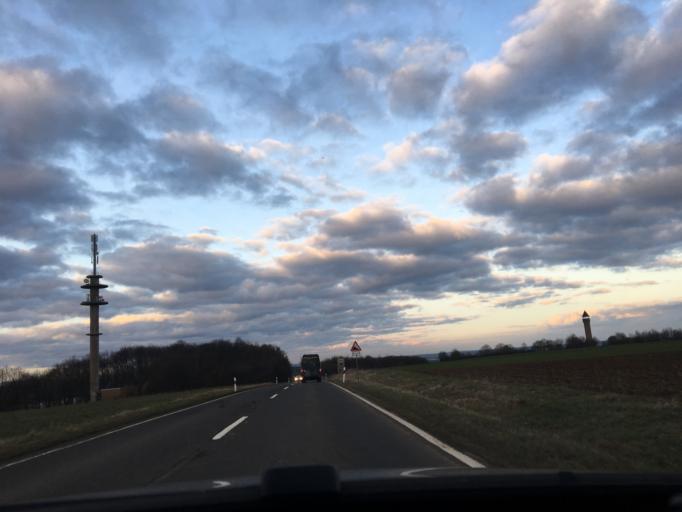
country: DE
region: Rheinland-Pfalz
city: Kettenheim
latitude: 49.7312
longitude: 8.1039
